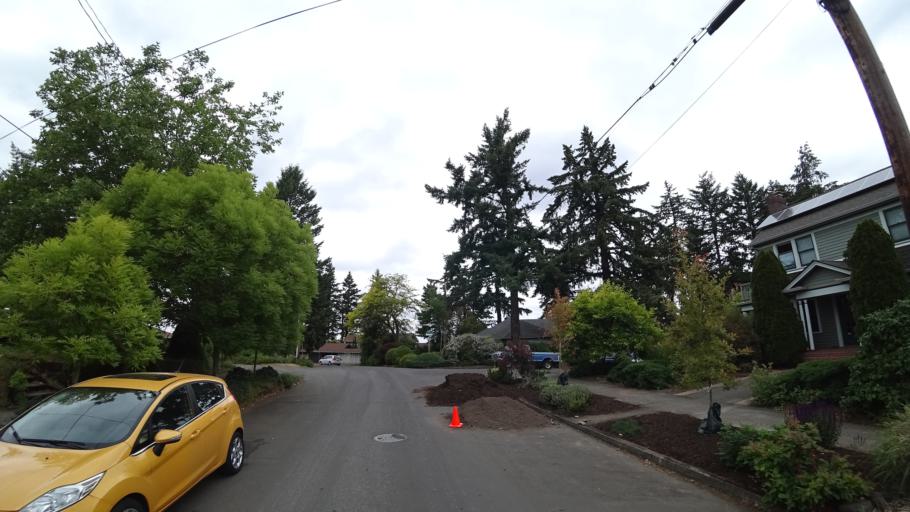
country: US
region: Oregon
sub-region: Multnomah County
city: Lents
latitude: 45.5201
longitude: -122.5923
